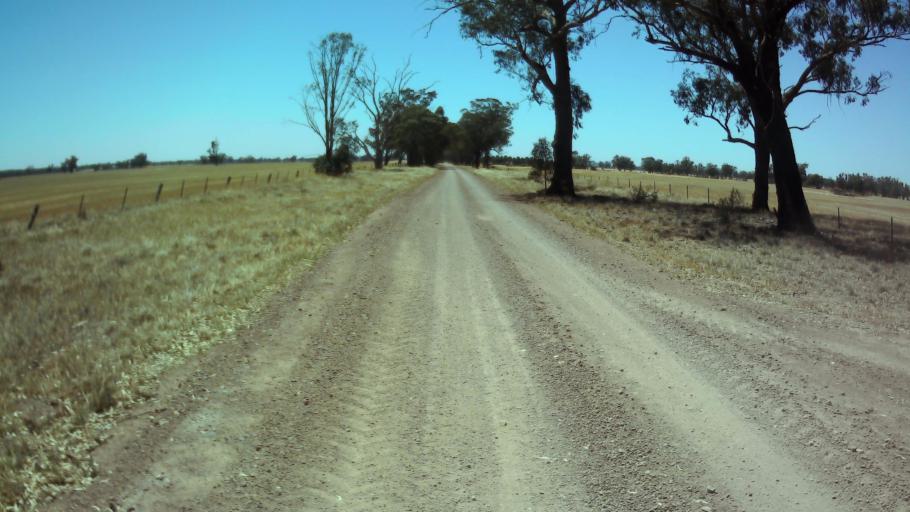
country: AU
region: New South Wales
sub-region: Weddin
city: Grenfell
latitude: -34.0421
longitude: 148.0128
